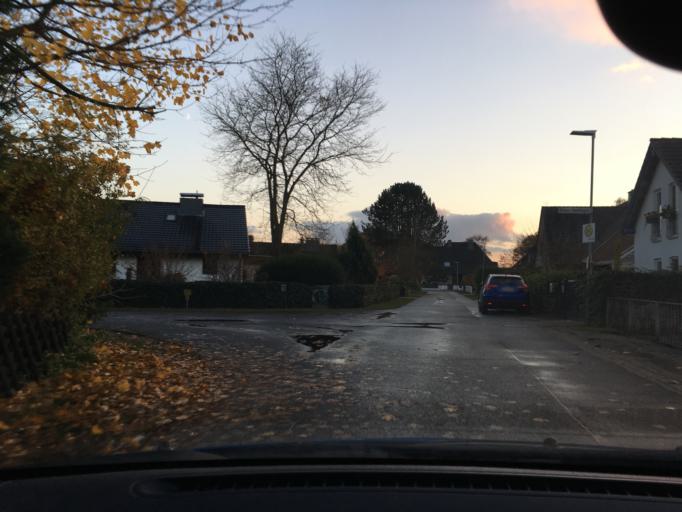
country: DE
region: Lower Saxony
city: Radbruch
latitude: 53.3358
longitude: 10.3064
